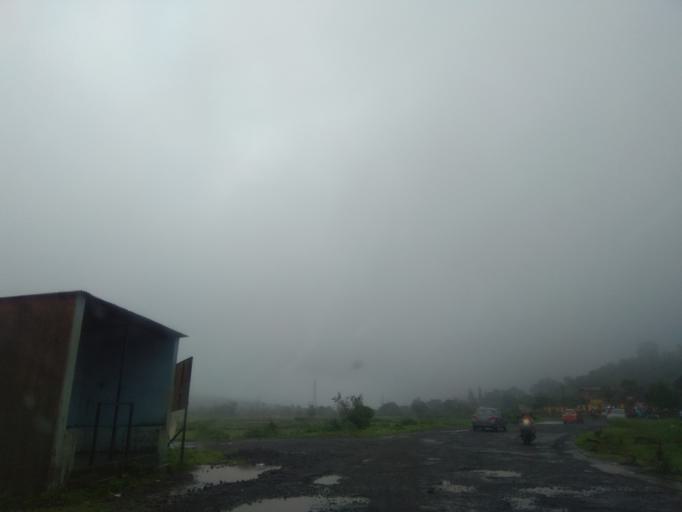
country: IN
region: Maharashtra
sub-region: Raigarh
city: Indapur
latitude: 18.4908
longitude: 73.4289
